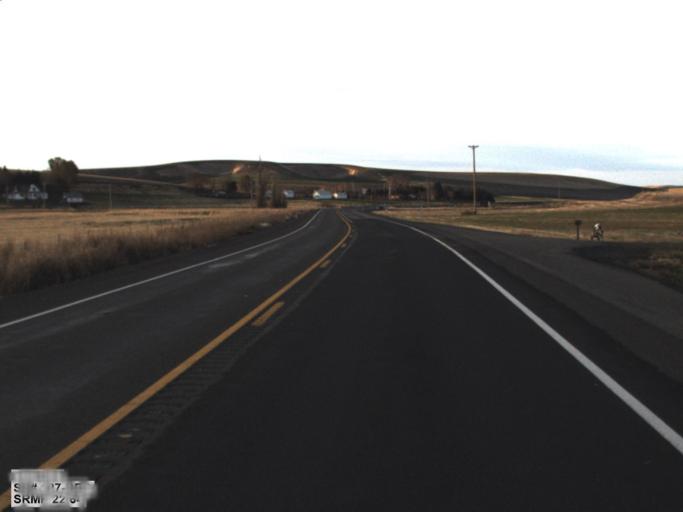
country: US
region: Washington
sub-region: Garfield County
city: Pomeroy
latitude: 46.7630
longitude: -117.7130
